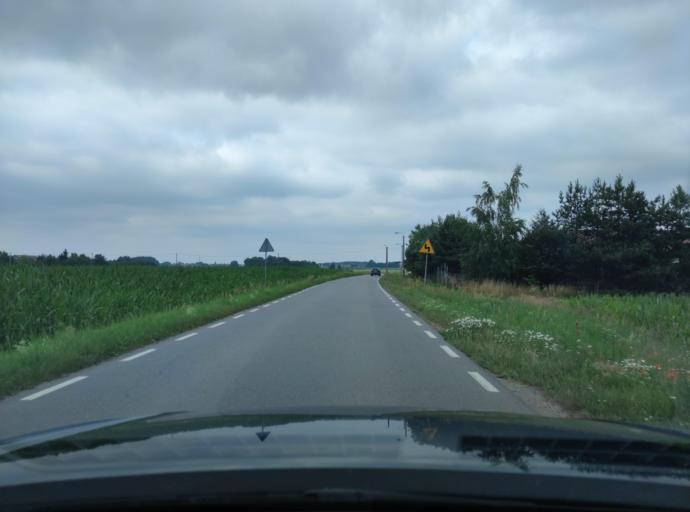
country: PL
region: Lower Silesian Voivodeship
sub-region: Powiat wroclawski
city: Kobierzyce
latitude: 50.9836
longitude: 16.9071
